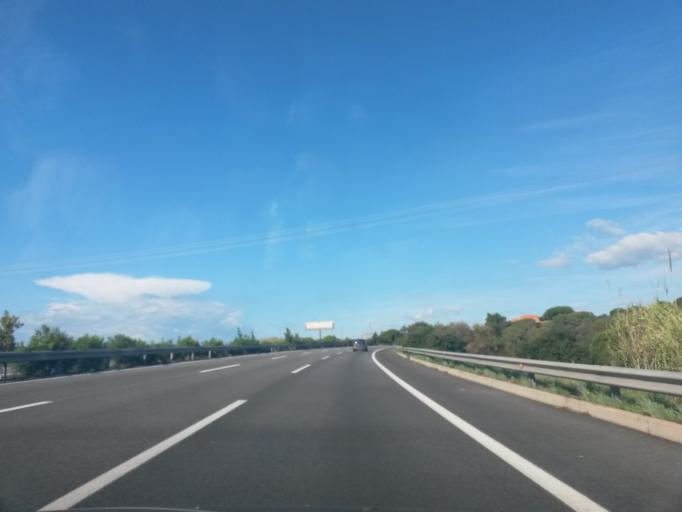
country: ES
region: Catalonia
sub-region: Provincia de Barcelona
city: Arenys de Mar
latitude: 41.5919
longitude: 2.5591
